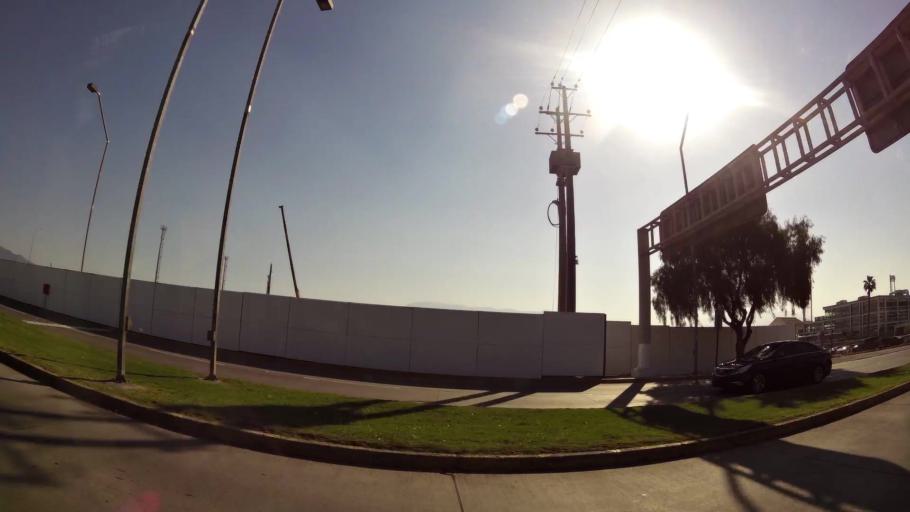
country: CL
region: Santiago Metropolitan
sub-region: Provincia de Santiago
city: Lo Prado
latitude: -33.3996
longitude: -70.7950
